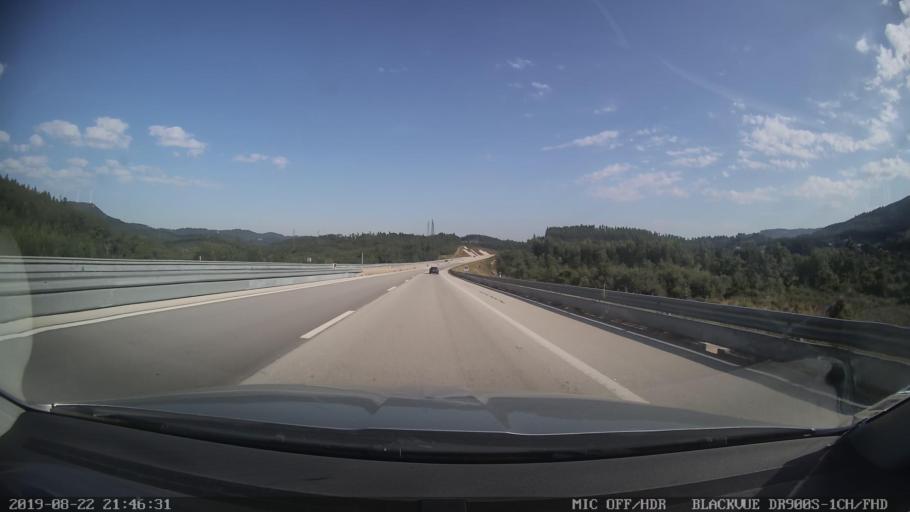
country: PT
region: Coimbra
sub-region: Penela
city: Penela
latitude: 39.9896
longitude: -8.3618
